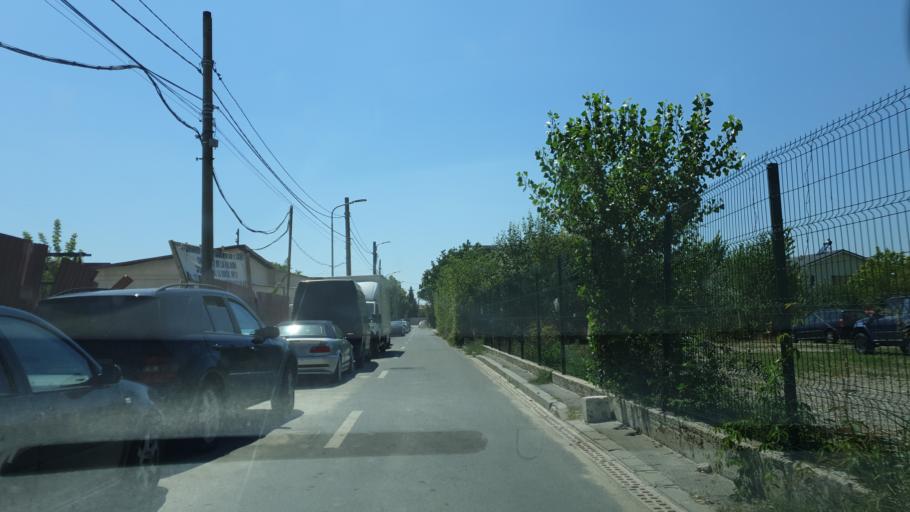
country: RO
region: Ilfov
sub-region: Comuna Chiajna
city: Rosu
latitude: 44.4683
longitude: 26.0234
